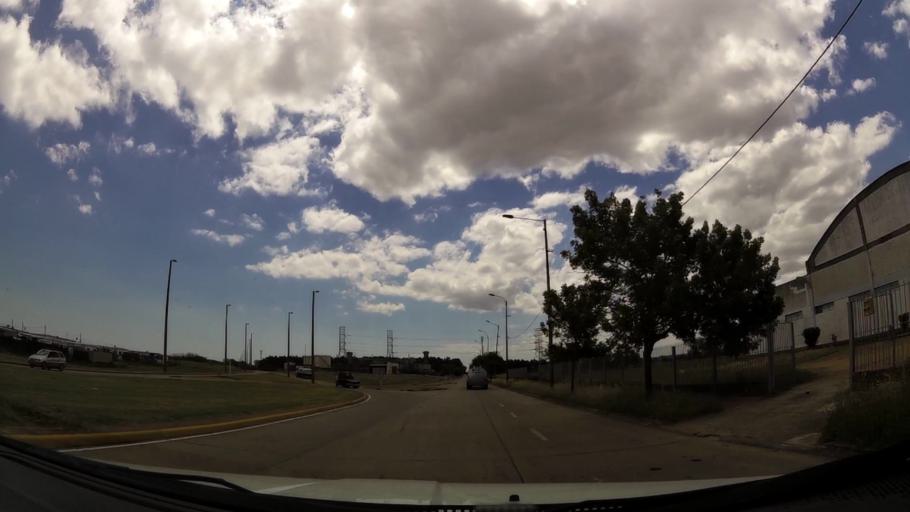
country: UY
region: Canelones
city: La Paz
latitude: -34.8282
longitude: -56.2324
